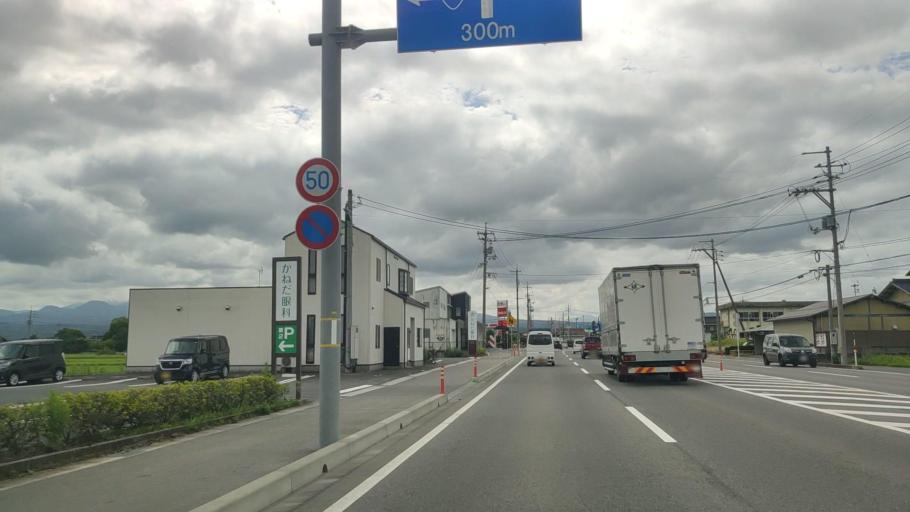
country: JP
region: Tottori
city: Yonago
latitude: 35.3990
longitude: 133.3774
